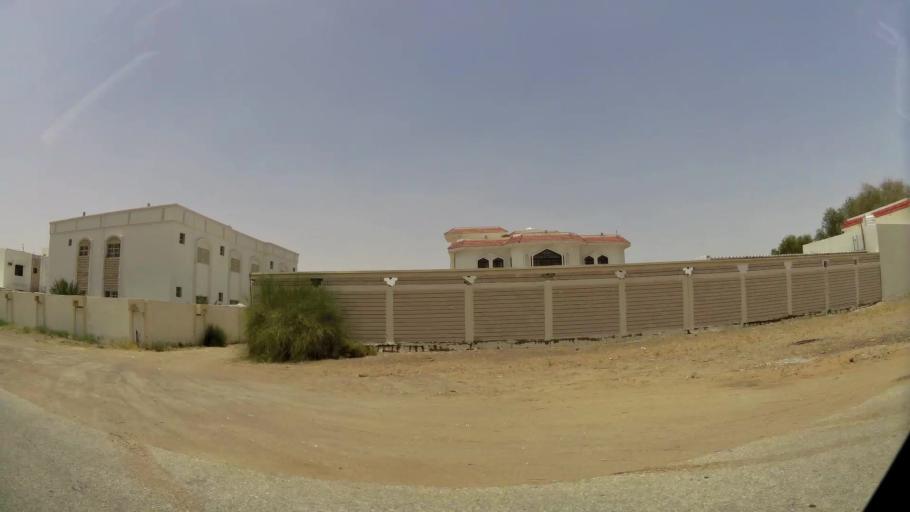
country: AE
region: Abu Dhabi
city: Al Ain
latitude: 24.2095
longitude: 55.7295
